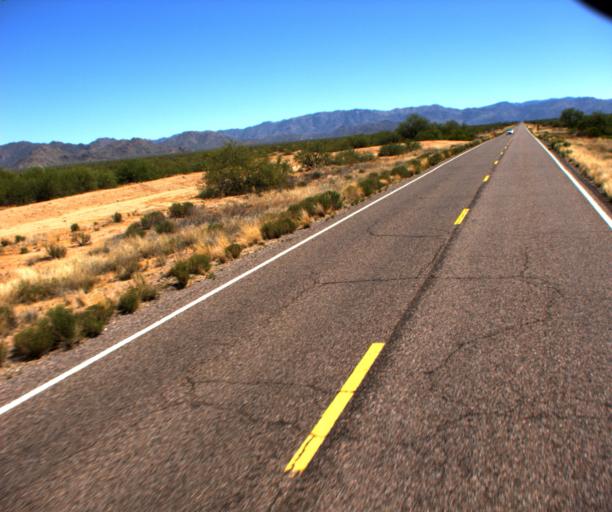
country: US
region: Arizona
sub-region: Yavapai County
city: Congress
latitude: 34.1289
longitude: -112.9366
